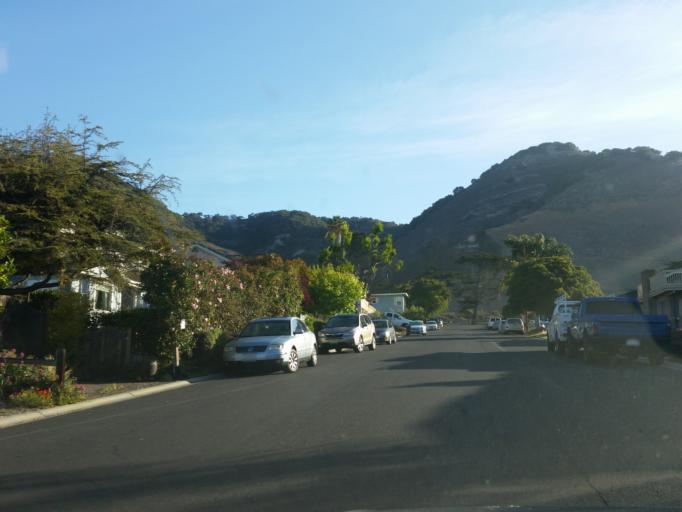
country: US
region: California
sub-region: San Luis Obispo County
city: Pismo Beach
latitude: 35.1581
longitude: -120.6771
